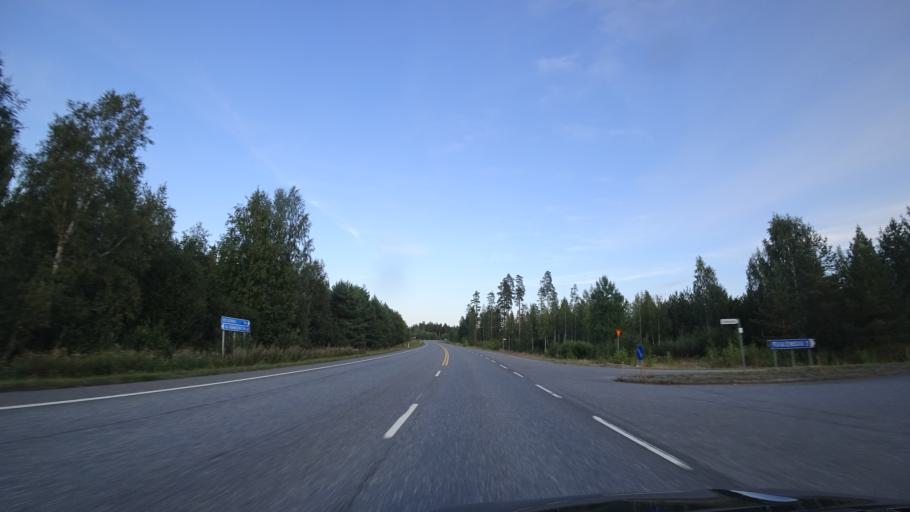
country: FI
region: Haeme
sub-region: Haemeenlinna
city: Janakkala
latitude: 60.8591
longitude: 24.5914
